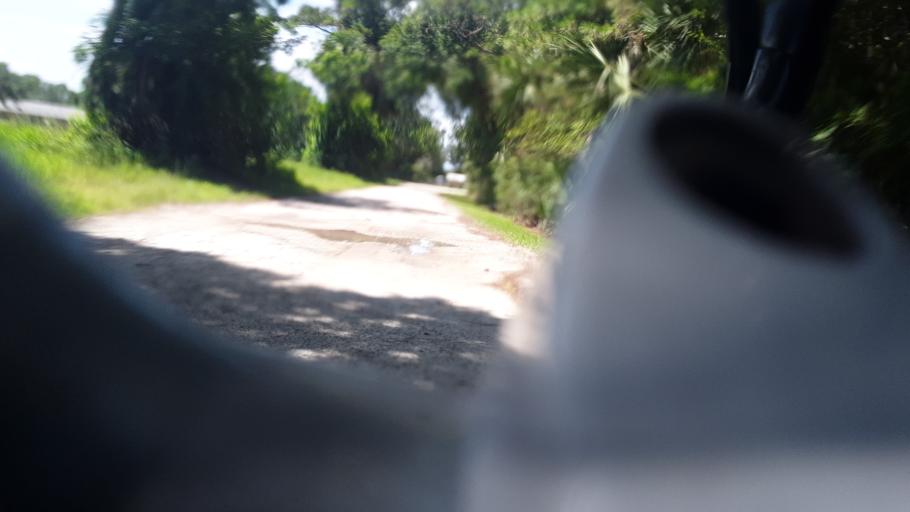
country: US
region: Florida
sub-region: Brevard County
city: Palm Bay
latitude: 27.9924
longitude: -80.6140
